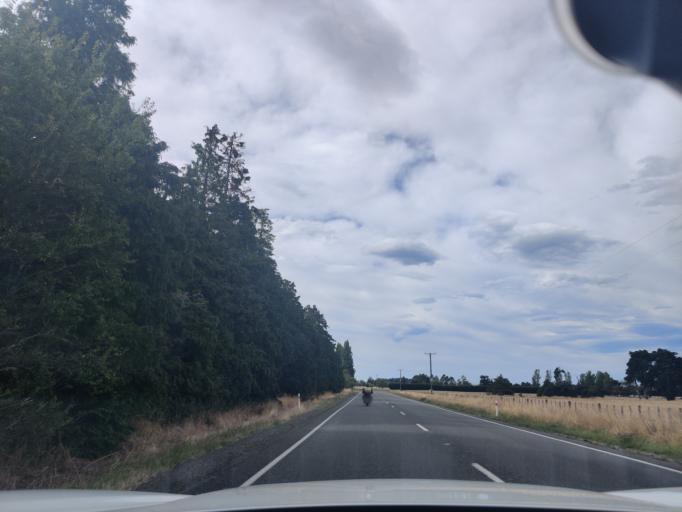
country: NZ
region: Wellington
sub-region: Masterton District
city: Masterton
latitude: -40.8641
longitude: 175.6438
